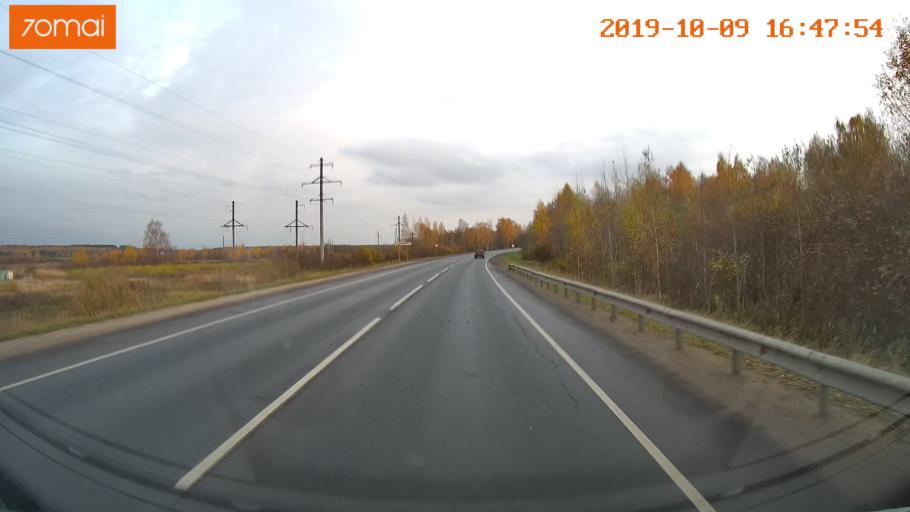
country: RU
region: Kostroma
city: Volgorechensk
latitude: 57.4335
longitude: 41.1848
